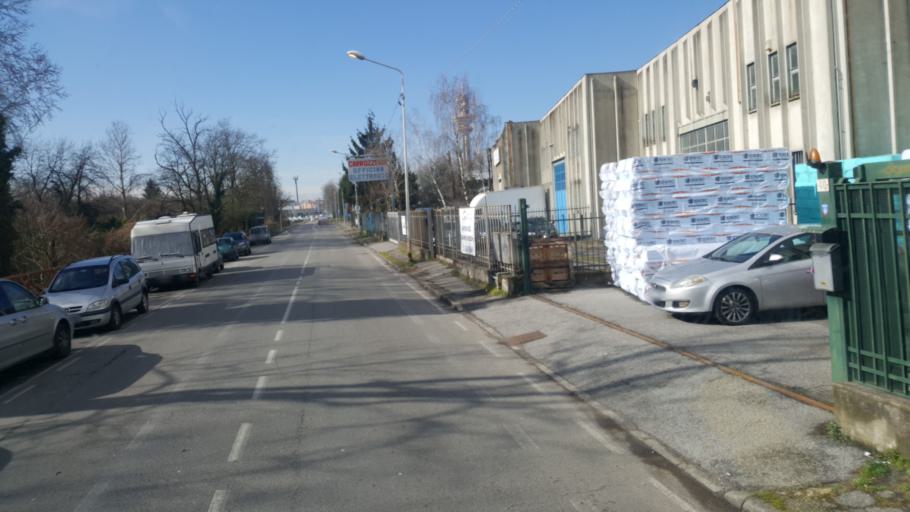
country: IT
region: Lombardy
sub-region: Citta metropolitana di Milano
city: Rozzano
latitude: 45.3770
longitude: 9.1740
